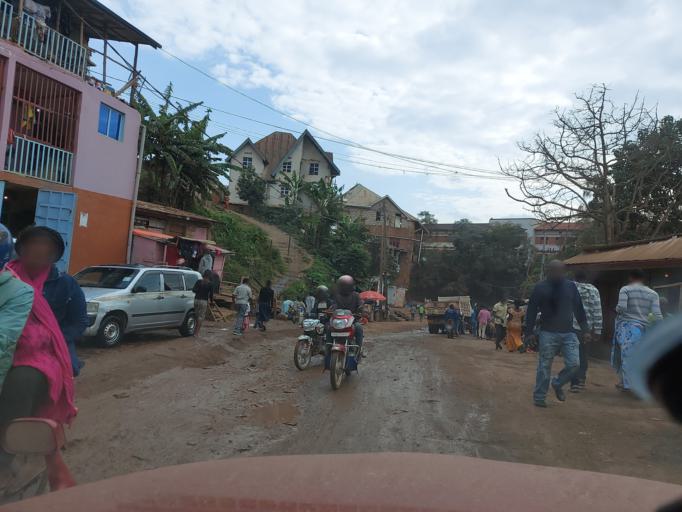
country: CD
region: South Kivu
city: Bukavu
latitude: -2.5082
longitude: 28.8482
